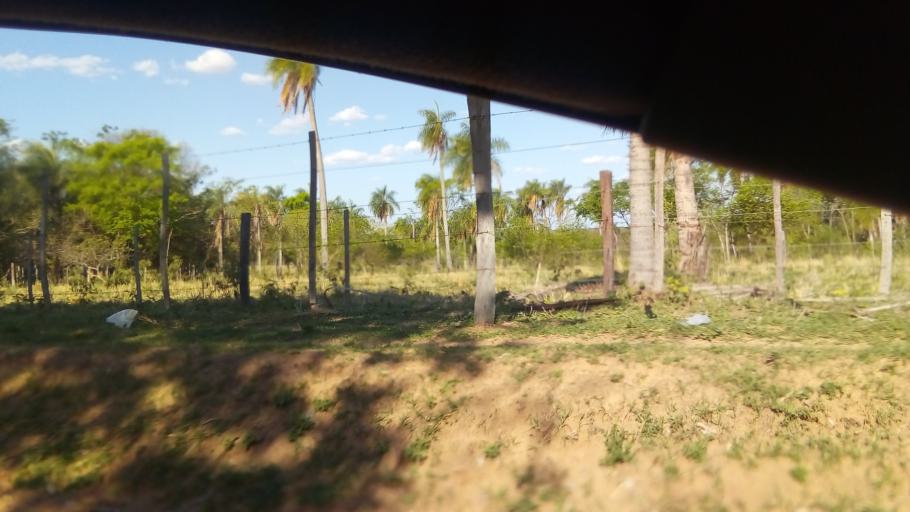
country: PY
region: Cordillera
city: Arroyos y Esteros
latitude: -24.9832
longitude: -57.1994
